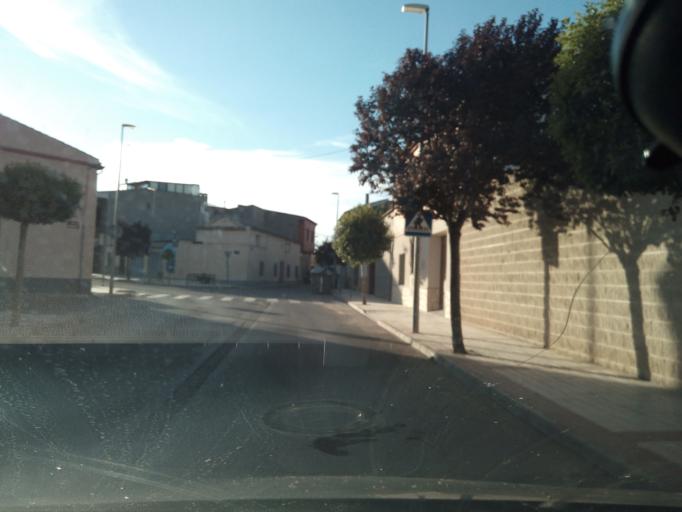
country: ES
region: Castille-La Mancha
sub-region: Province of Toledo
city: Villacanas
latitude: 39.6207
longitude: -3.3353
